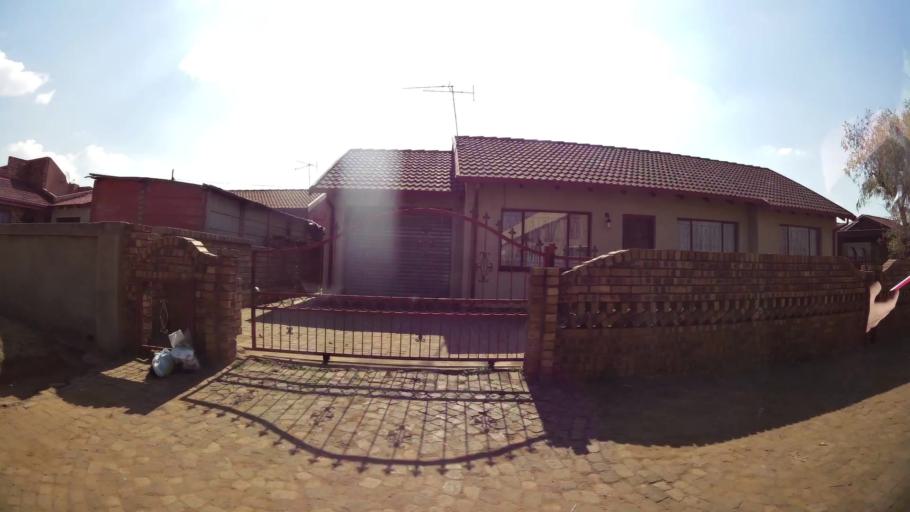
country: ZA
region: Gauteng
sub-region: Ekurhuleni Metropolitan Municipality
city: Benoni
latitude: -26.1493
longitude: 28.3996
